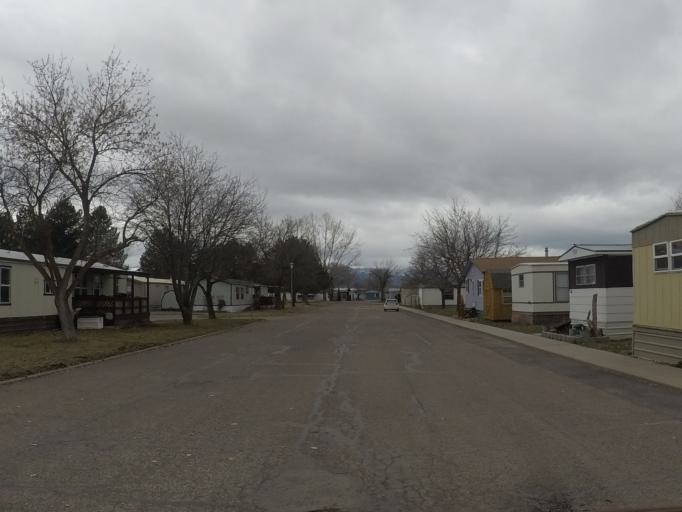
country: US
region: Montana
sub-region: Missoula County
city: Missoula
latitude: 46.8875
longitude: -114.0196
